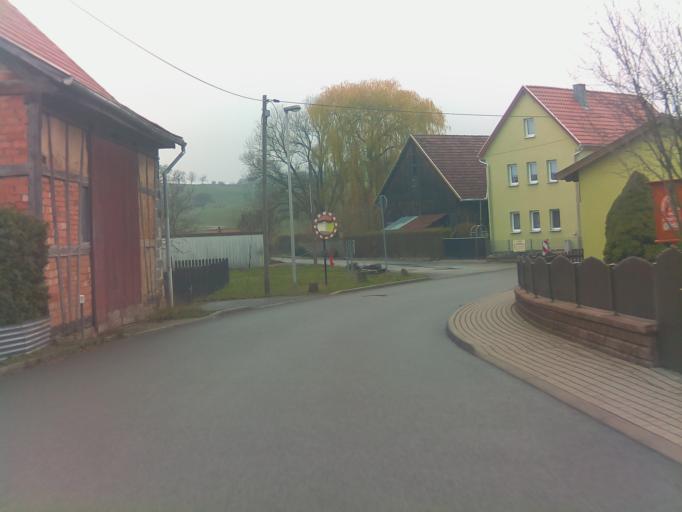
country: DE
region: Thuringia
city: Juchsen
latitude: 50.4312
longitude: 10.4941
